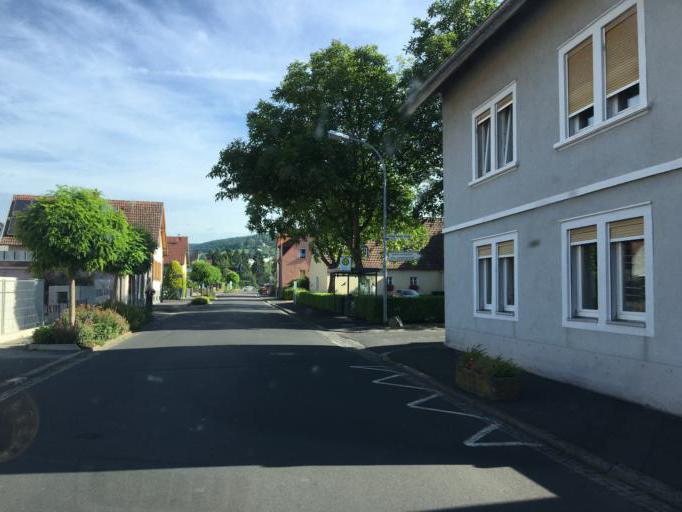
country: DE
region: Bavaria
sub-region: Regierungsbezirk Unterfranken
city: Margetshochheim
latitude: 49.8352
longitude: 9.8720
